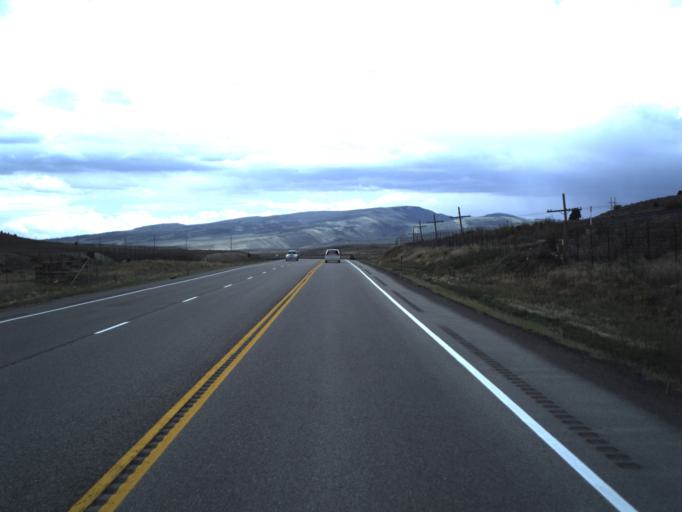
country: US
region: Utah
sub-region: Carbon County
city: Helper
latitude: 39.8950
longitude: -111.0534
